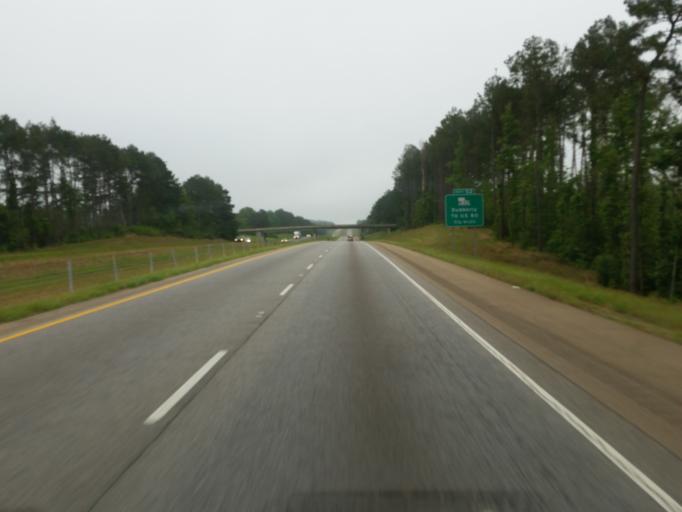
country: US
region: Louisiana
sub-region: Webster Parish
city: Minden
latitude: 32.5769
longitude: -93.2312
